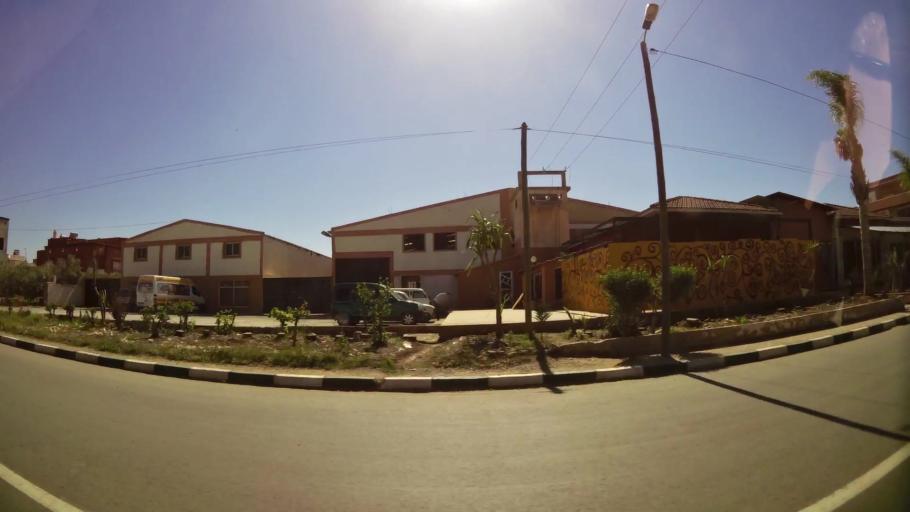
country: MA
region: Oriental
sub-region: Berkane-Taourirt
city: Berkane
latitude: 34.9436
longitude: -2.3260
